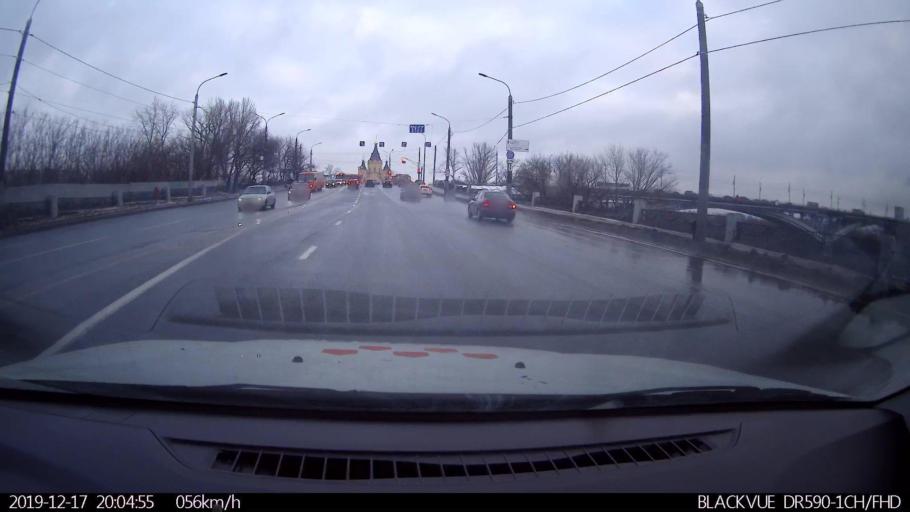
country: RU
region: Nizjnij Novgorod
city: Nizhniy Novgorod
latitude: 56.3277
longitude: 43.9681
